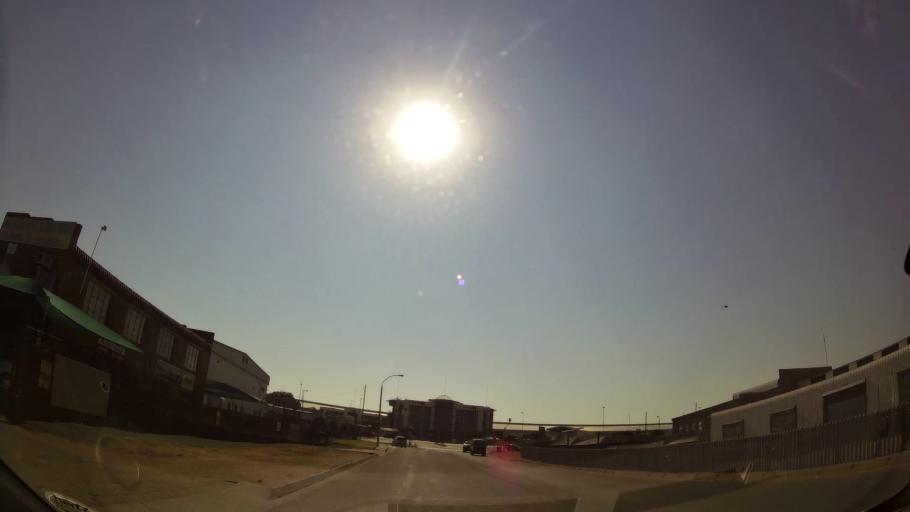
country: ZA
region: Gauteng
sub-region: Ekurhuleni Metropolitan Municipality
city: Boksburg
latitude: -26.1667
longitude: 28.2335
